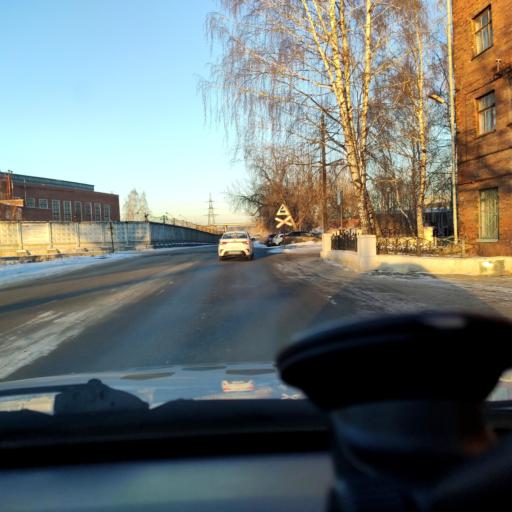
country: RU
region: Perm
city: Perm
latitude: 58.0388
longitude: 56.3091
